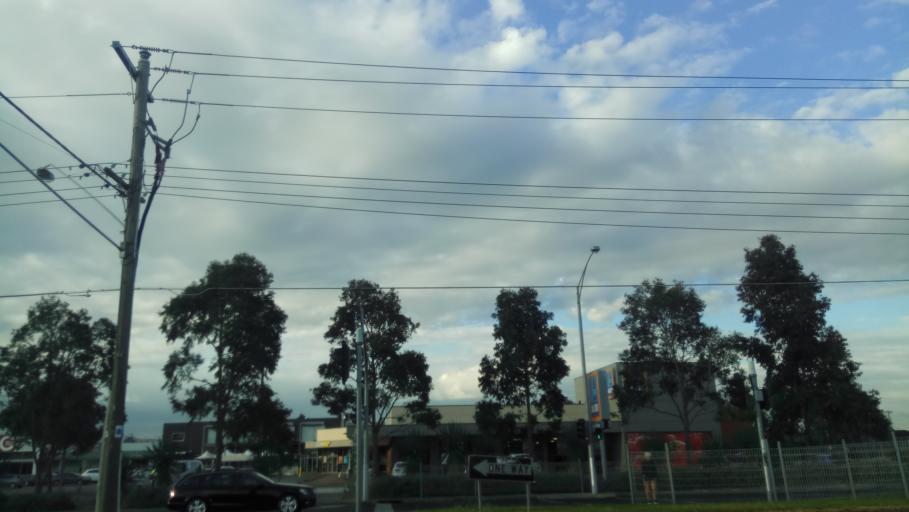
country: AU
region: Victoria
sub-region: Hobsons Bay
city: Laverton
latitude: -37.8712
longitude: 144.7754
